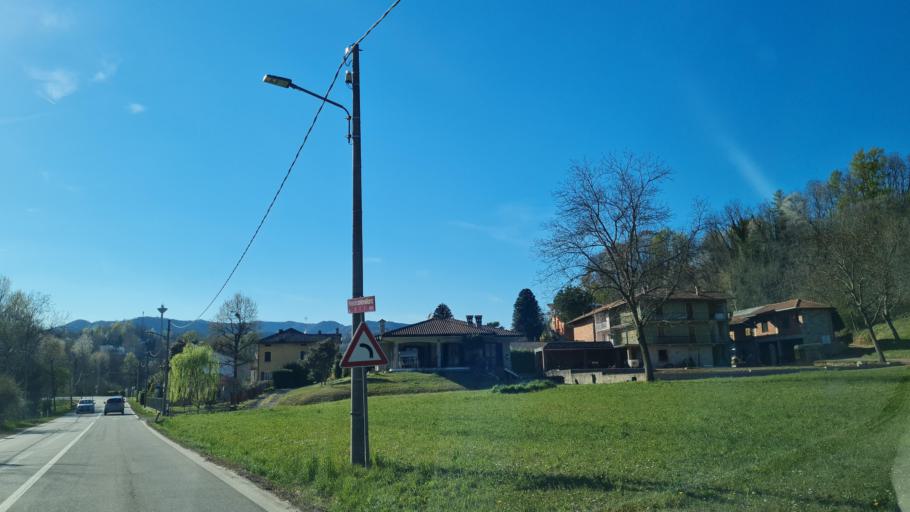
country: IT
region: Piedmont
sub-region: Provincia di Novara
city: Maggiora
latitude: 45.6942
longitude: 8.4291
